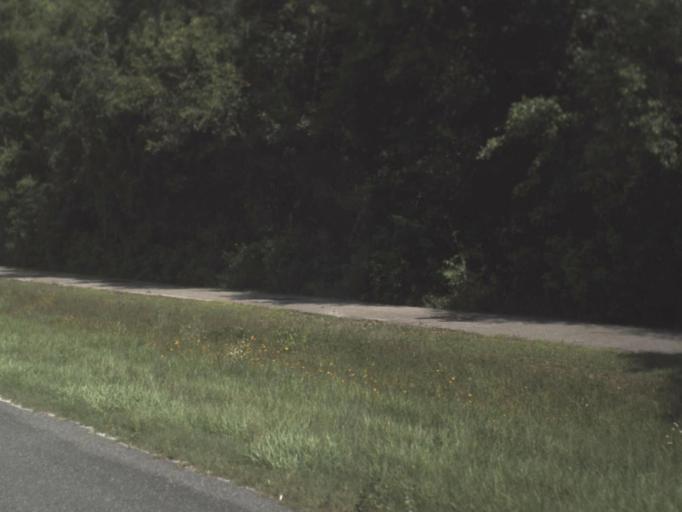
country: US
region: Florida
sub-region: Suwannee County
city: Wellborn
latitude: 29.9524
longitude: -82.8592
